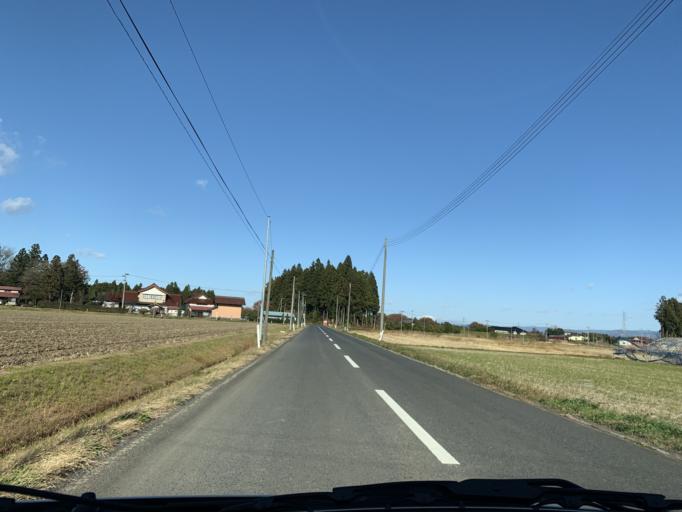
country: JP
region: Iwate
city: Mizusawa
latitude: 39.0779
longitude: 141.1208
